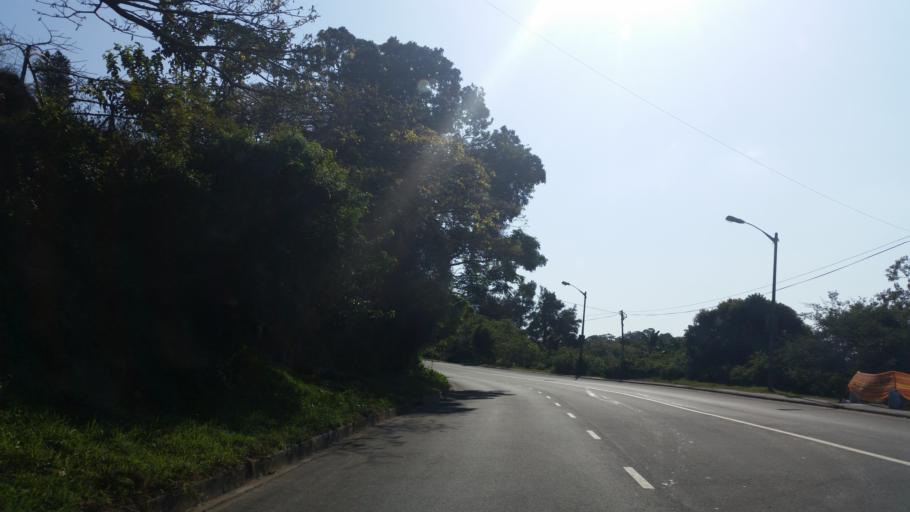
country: ZA
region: KwaZulu-Natal
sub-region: eThekwini Metropolitan Municipality
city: Berea
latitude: -29.8268
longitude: 30.9131
